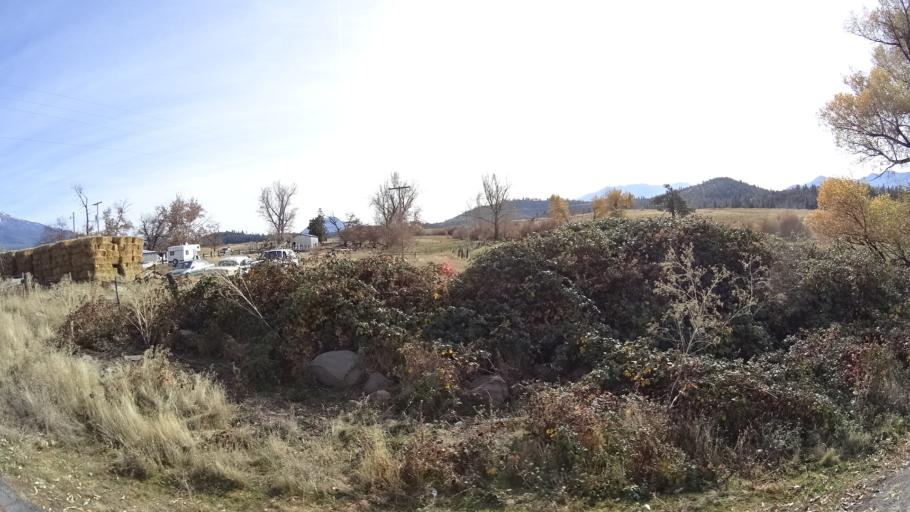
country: US
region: California
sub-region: Siskiyou County
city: Weed
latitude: 41.4652
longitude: -122.3879
